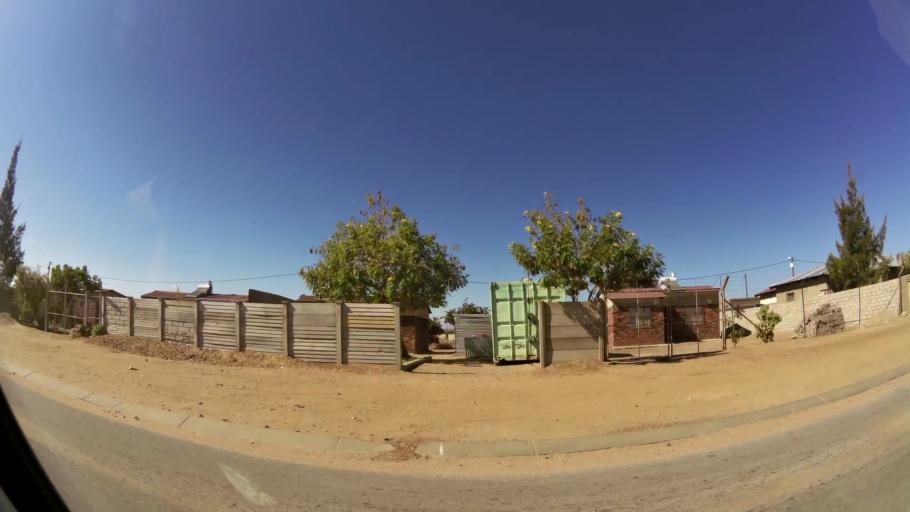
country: ZA
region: Limpopo
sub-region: Capricorn District Municipality
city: Polokwane
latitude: -23.8557
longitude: 29.4133
